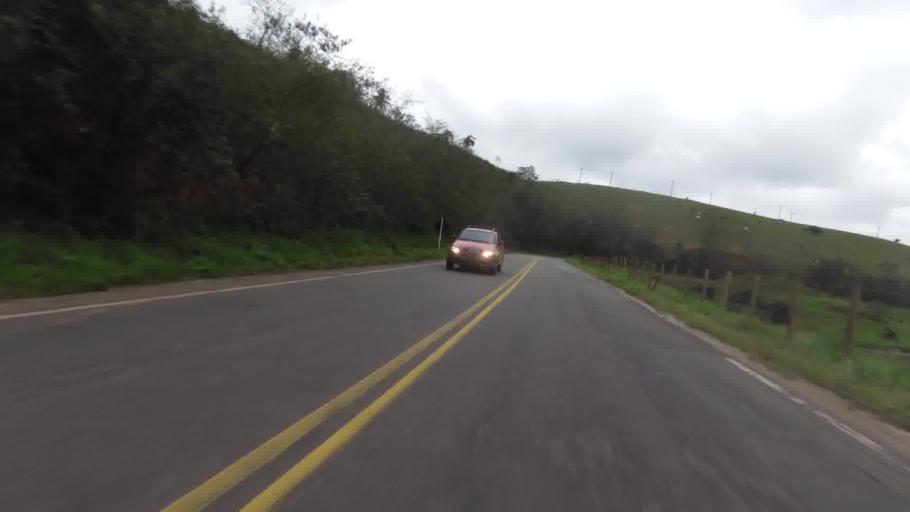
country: BR
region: Espirito Santo
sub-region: Alfredo Chaves
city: Alfredo Chaves
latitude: -20.6682
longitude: -40.7072
